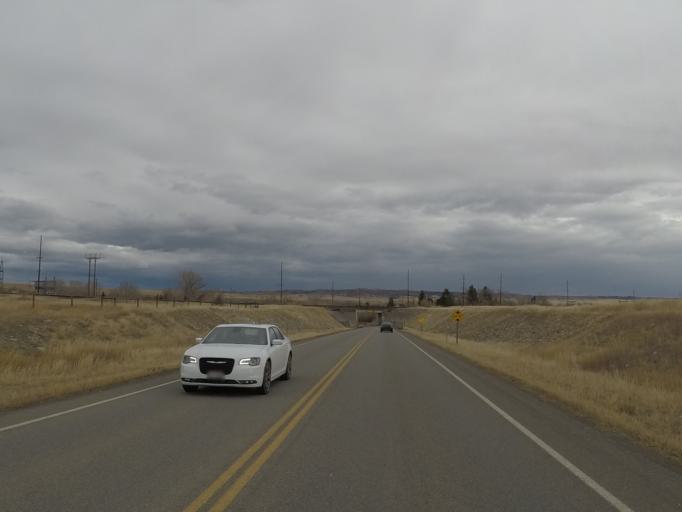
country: US
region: Montana
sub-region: Sweet Grass County
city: Big Timber
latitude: 45.8431
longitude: -109.9417
